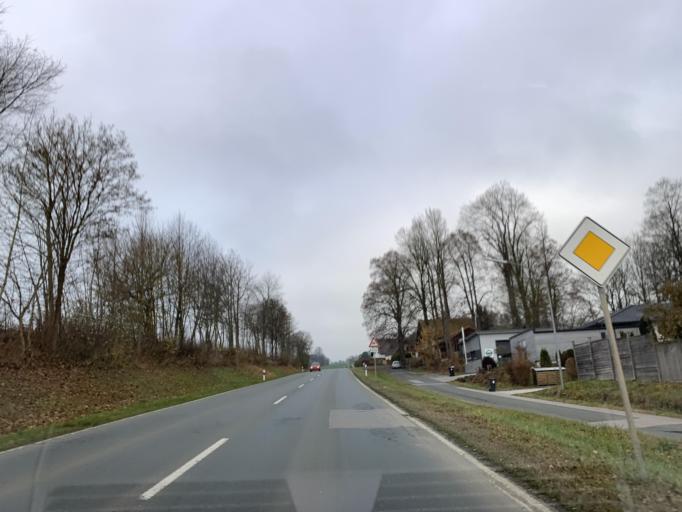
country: DE
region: Bavaria
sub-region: Upper Palatinate
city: Roetz
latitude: 49.3434
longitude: 12.5176
